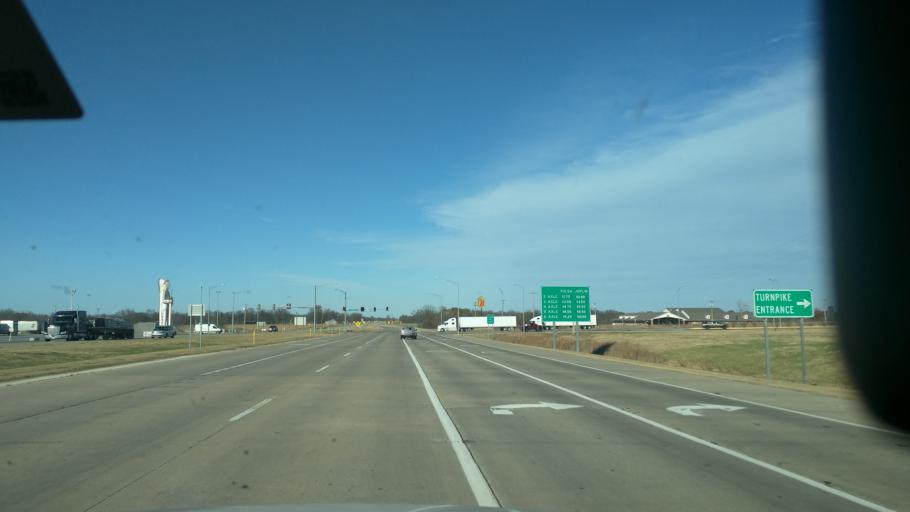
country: US
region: Oklahoma
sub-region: Craig County
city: Vinita
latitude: 36.5656
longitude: -95.2200
